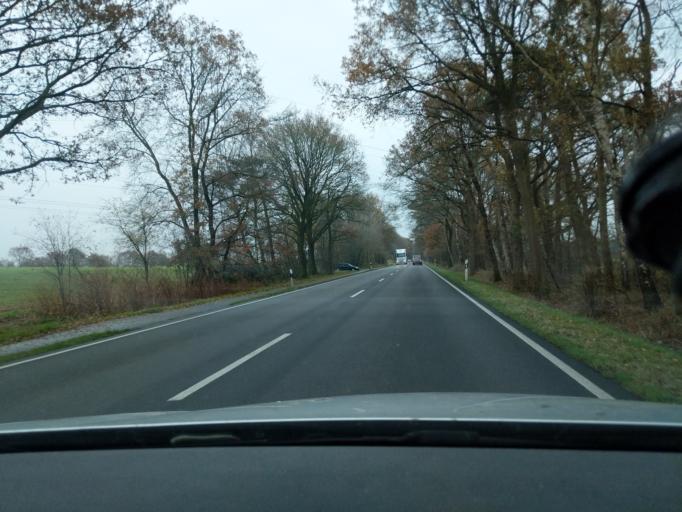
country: DE
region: Lower Saxony
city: Gyhum
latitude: 53.2238
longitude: 9.2923
